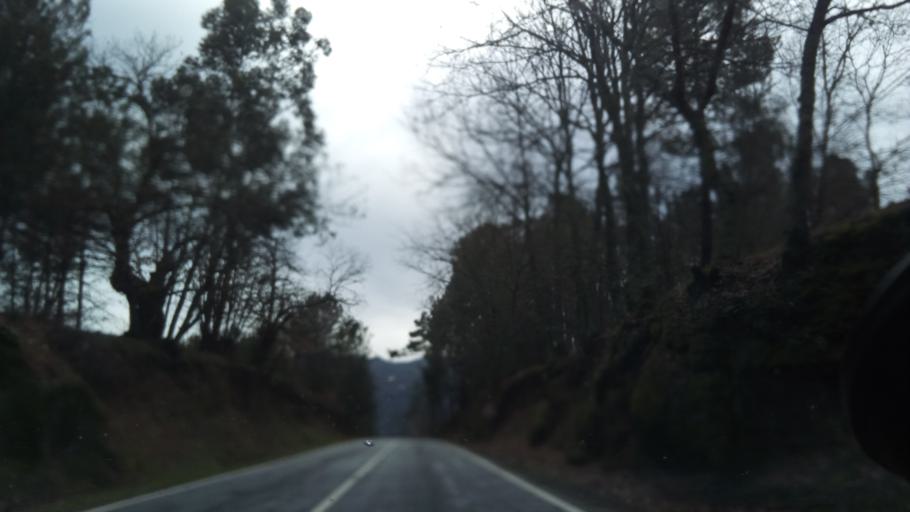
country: PT
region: Guarda
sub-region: Seia
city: Seia
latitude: 40.4433
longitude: -7.7106
